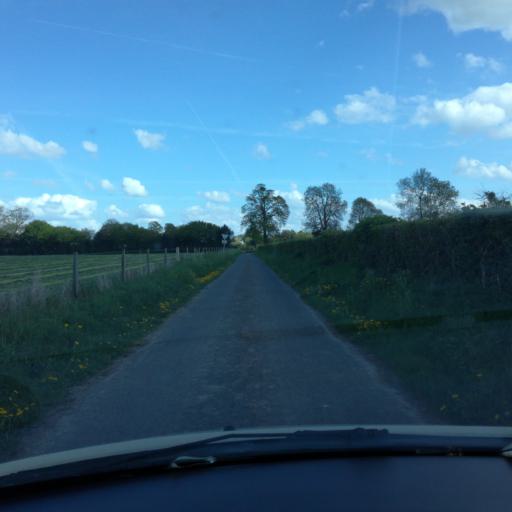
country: FR
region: Picardie
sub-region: Departement de la Somme
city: Hornoy-le-Bourg
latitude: 49.8317
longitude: 1.9306
